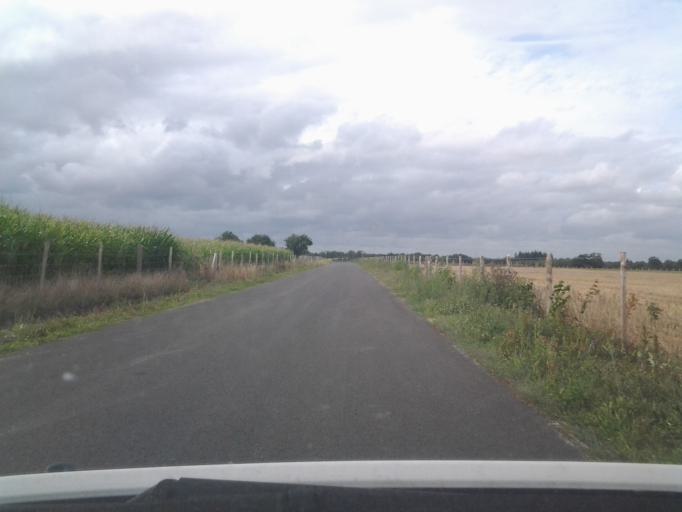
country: FR
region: Pays de la Loire
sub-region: Departement de la Vendee
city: Dompierre-sur-Yon
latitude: 46.7000
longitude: -1.3627
